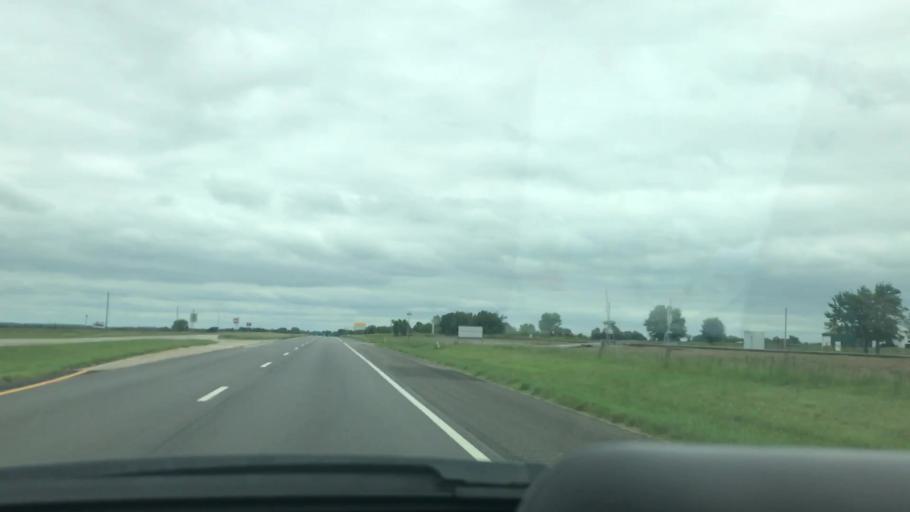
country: US
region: Oklahoma
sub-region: Mayes County
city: Pryor
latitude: 36.4516
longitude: -95.2658
